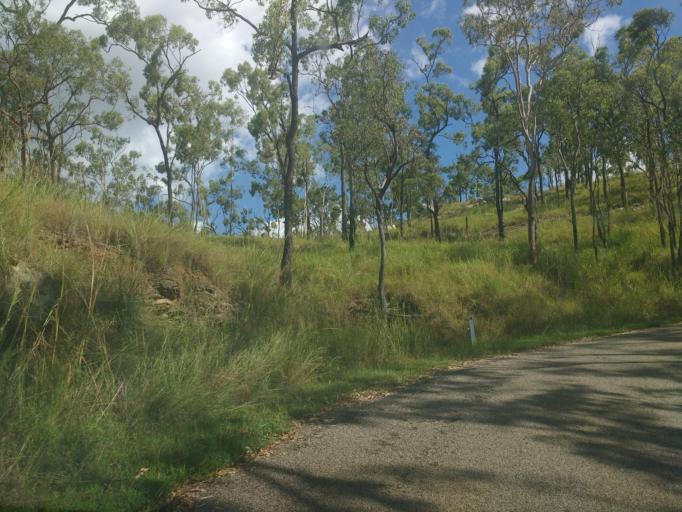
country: AU
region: Queensland
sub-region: Townsville
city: Townsville
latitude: -19.3576
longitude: 146.8117
